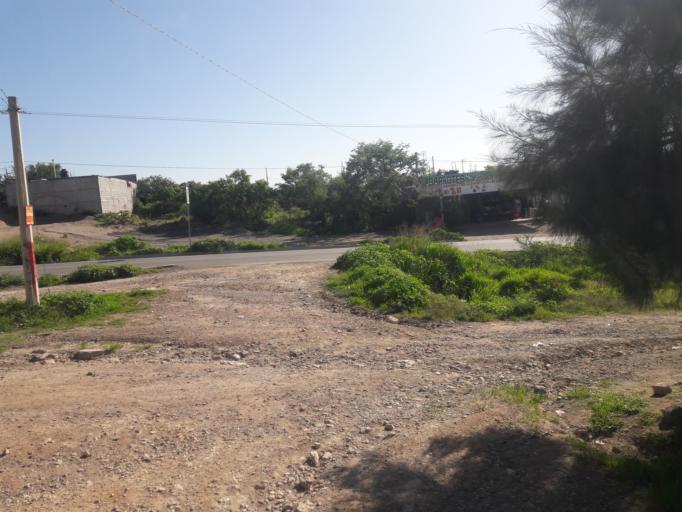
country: MX
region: Oaxaca
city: Ciudad de Huajuapam de Leon
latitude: 17.8057
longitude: -97.8057
